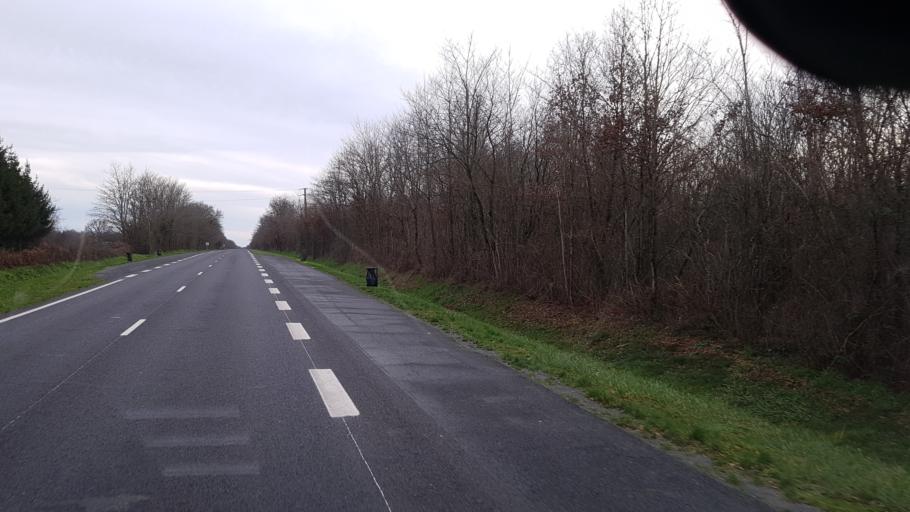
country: FR
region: Centre
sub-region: Departement du Loir-et-Cher
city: Nouan-le-Fuzelier
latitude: 47.4813
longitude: 2.0397
